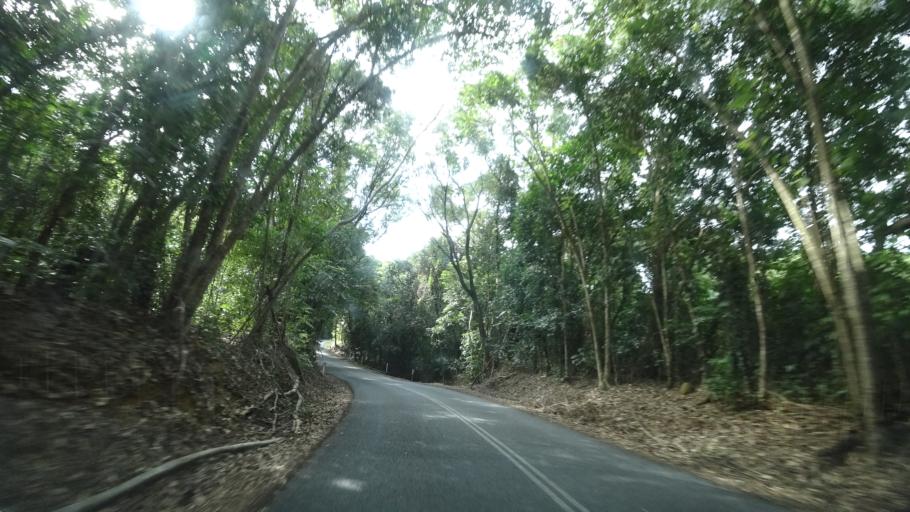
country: AU
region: Queensland
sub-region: Cairns
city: Port Douglas
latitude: -16.0997
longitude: 145.4589
